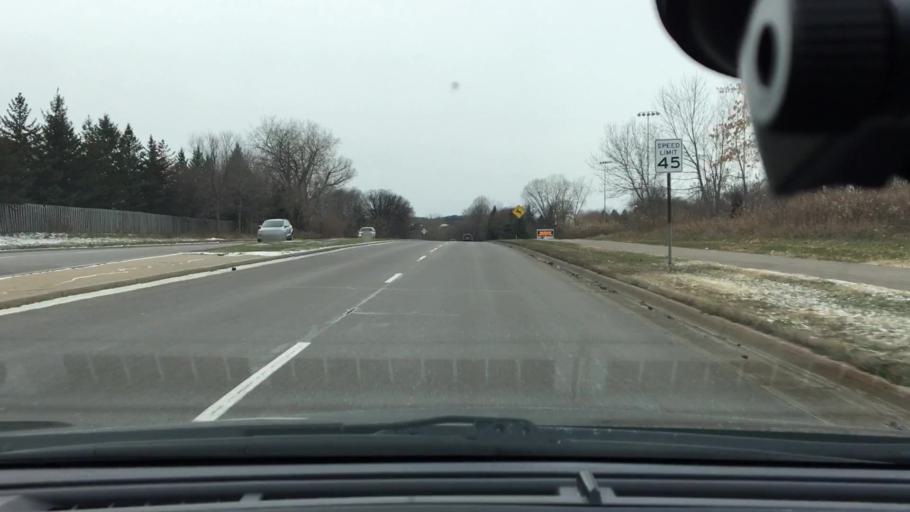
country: US
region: Minnesota
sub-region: Hennepin County
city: New Hope
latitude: 45.0333
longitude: -93.4222
